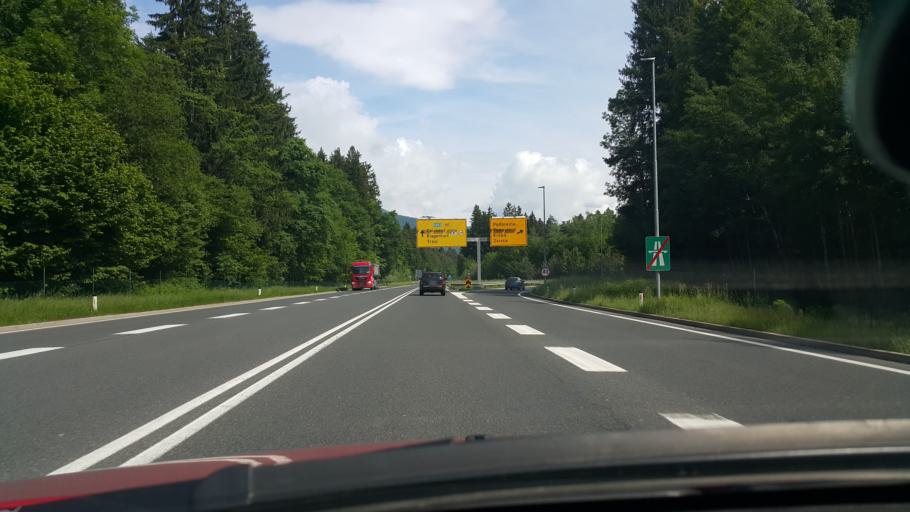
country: SI
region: Trzic
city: Bistrica pri Trzicu
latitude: 46.3140
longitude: 14.2786
